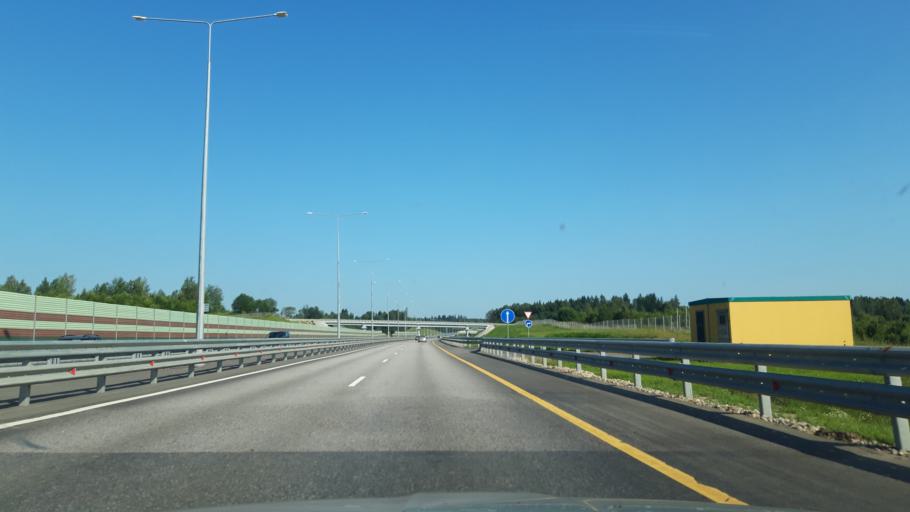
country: RU
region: Moskovskaya
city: Klin
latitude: 56.2337
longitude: 36.7551
